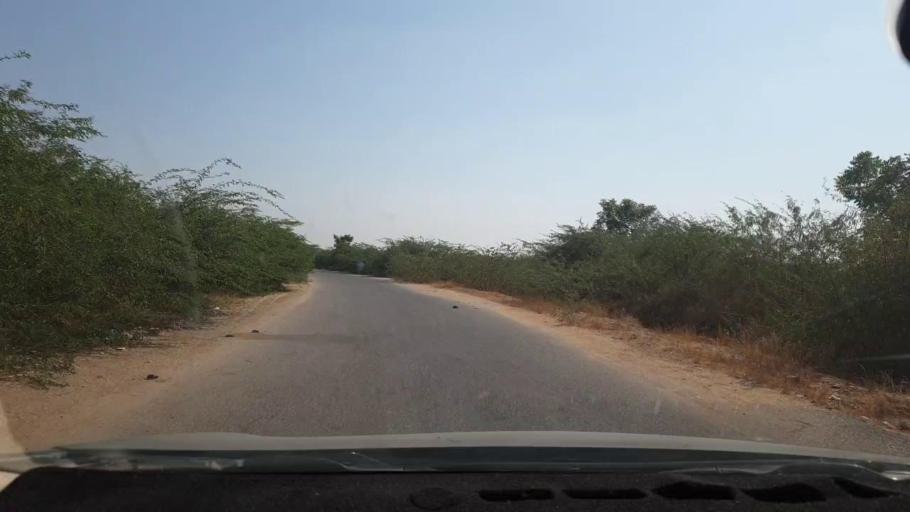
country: PK
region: Sindh
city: Malir Cantonment
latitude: 25.1425
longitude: 67.1944
